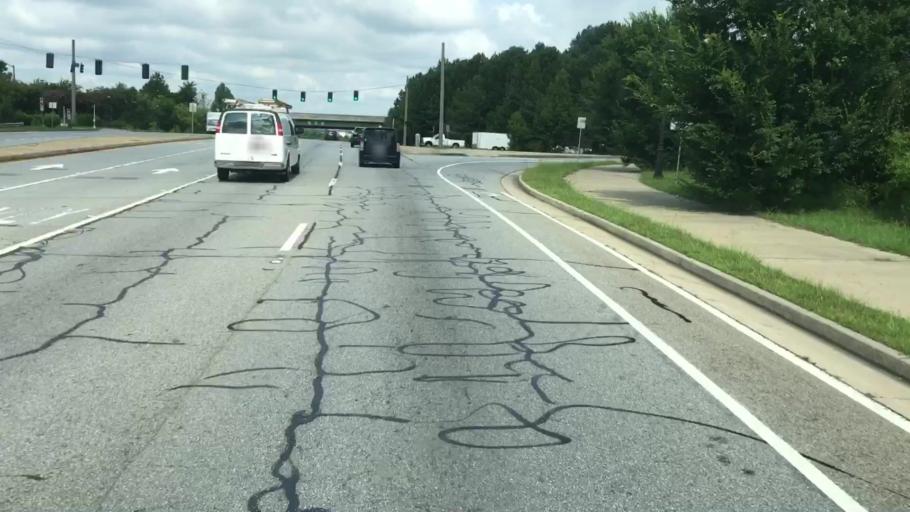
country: US
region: Georgia
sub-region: Gwinnett County
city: Suwanee
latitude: 33.9867
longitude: -84.0809
